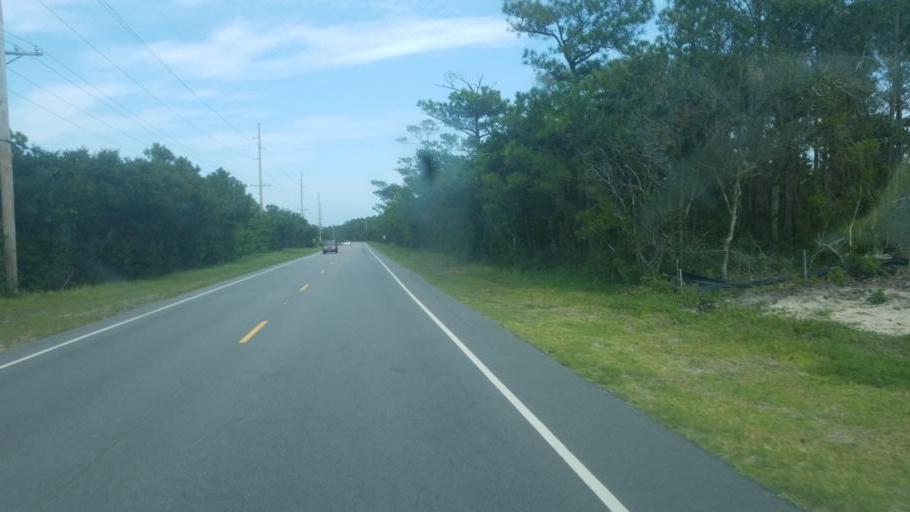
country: US
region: North Carolina
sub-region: Dare County
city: Buxton
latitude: 35.2530
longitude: -75.5969
